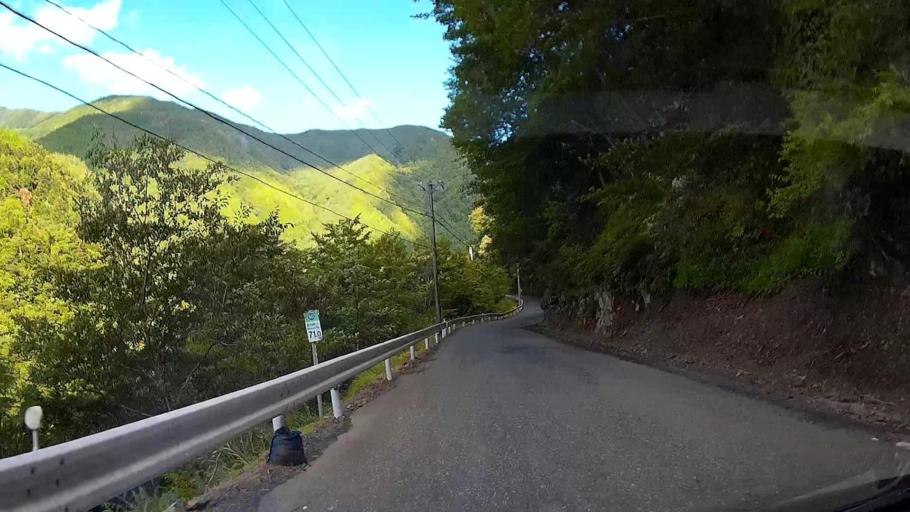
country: JP
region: Shizuoka
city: Shizuoka-shi
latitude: 35.2854
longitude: 138.2197
